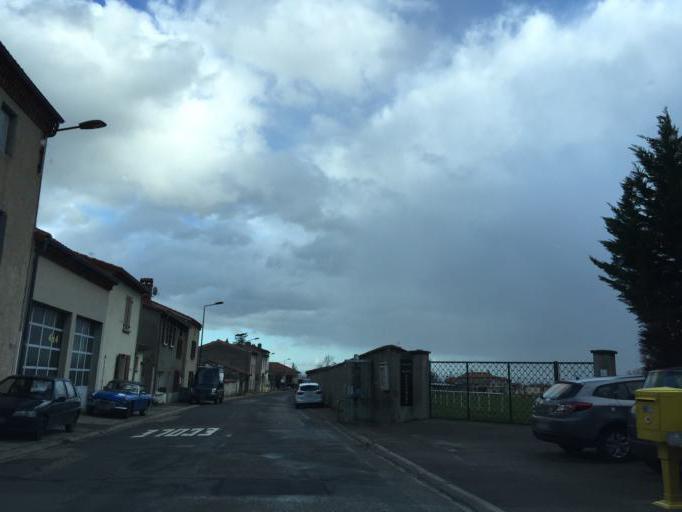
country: FR
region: Rhone-Alpes
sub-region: Departement de la Loire
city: Champdieu
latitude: 45.6457
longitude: 4.0482
